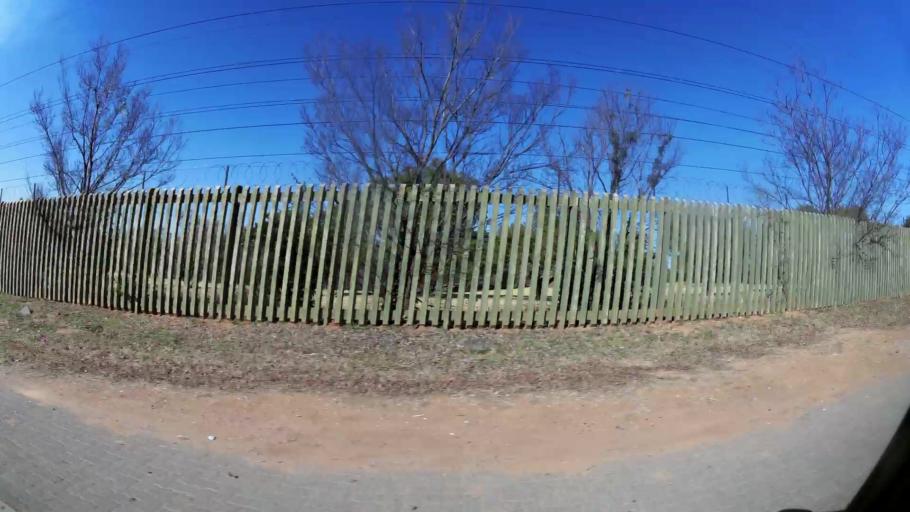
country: ZA
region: Gauteng
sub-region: City of Johannesburg Metropolitan Municipality
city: Roodepoort
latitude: -26.1017
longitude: 27.9643
